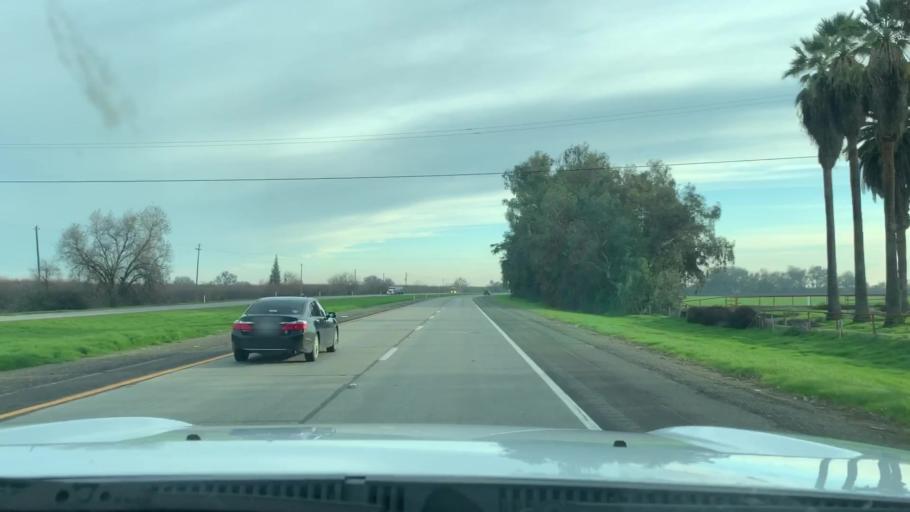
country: US
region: California
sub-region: Kings County
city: Lemoore
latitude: 36.3609
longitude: -119.8093
